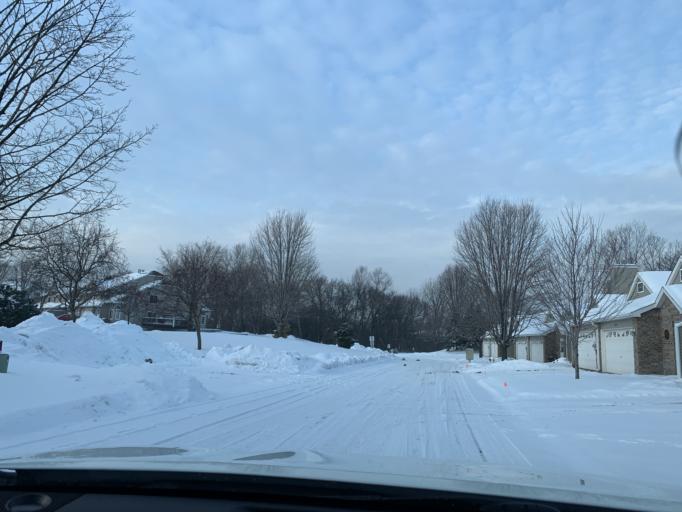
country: US
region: Minnesota
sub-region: Anoka County
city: Coon Rapids
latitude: 45.1647
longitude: -93.2897
